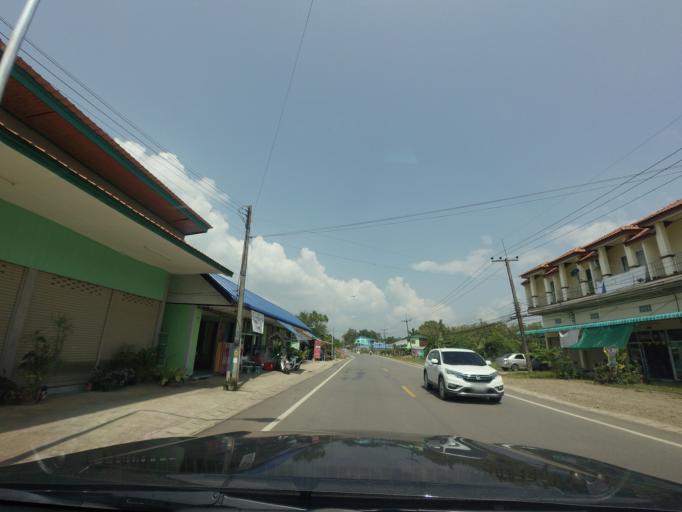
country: TH
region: Nan
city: Santi Suk
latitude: 18.9293
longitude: 100.9307
